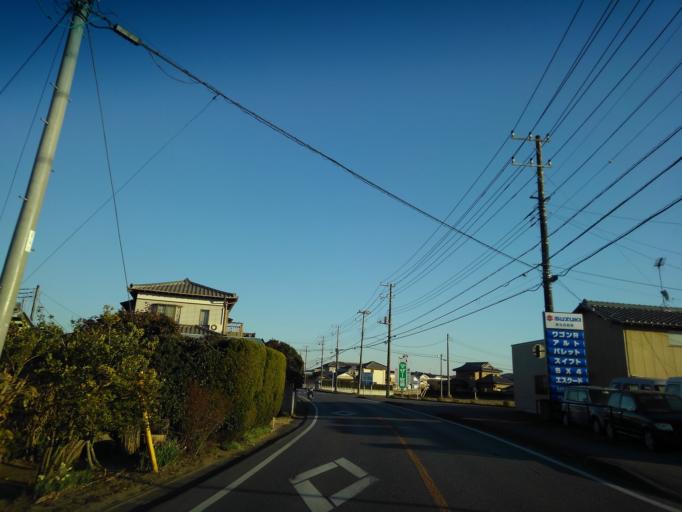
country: JP
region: Chiba
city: Kimitsu
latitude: 35.3093
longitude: 139.9394
